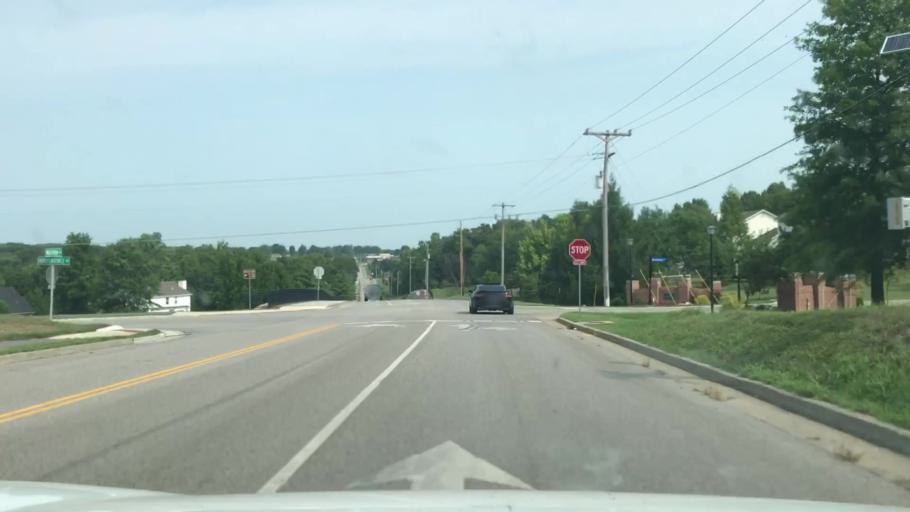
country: US
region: Missouri
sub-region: Saint Charles County
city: Cottleville
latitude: 38.7173
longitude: -90.6417
